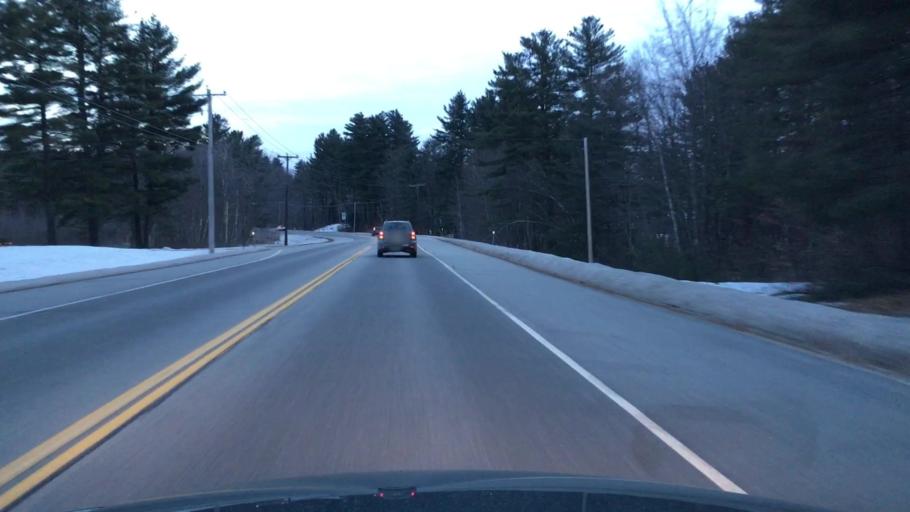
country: US
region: New Hampshire
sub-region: Merrimack County
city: Newbury
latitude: 43.2938
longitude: -71.9943
